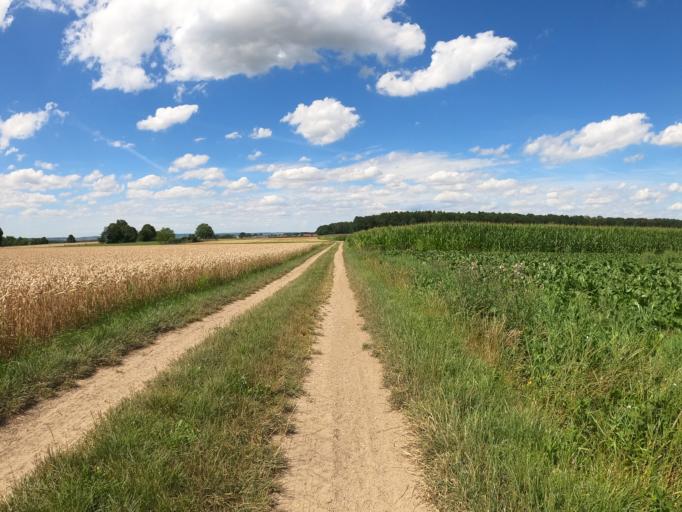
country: DE
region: Bavaria
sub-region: Swabia
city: Leipheim
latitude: 48.4005
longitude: 10.2044
